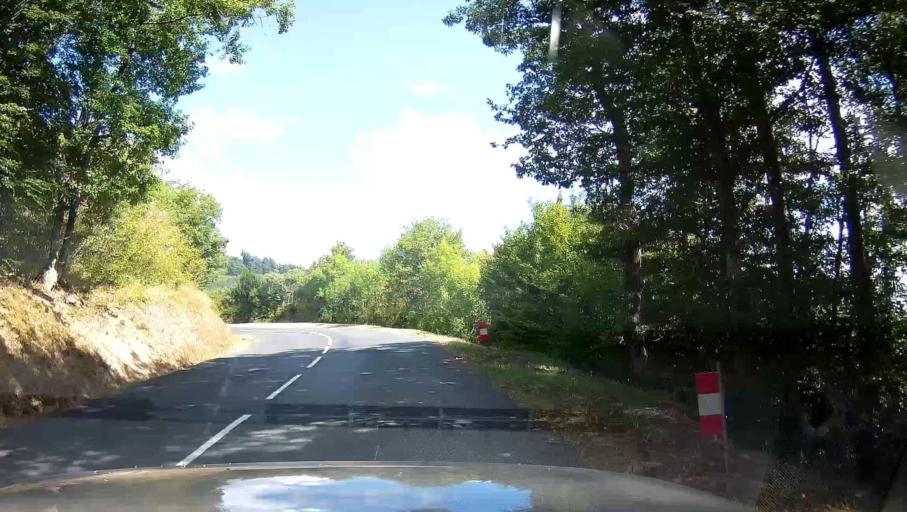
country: FR
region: Rhone-Alpes
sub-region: Departement du Rhone
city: Cogny
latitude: 45.9875
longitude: 4.5730
